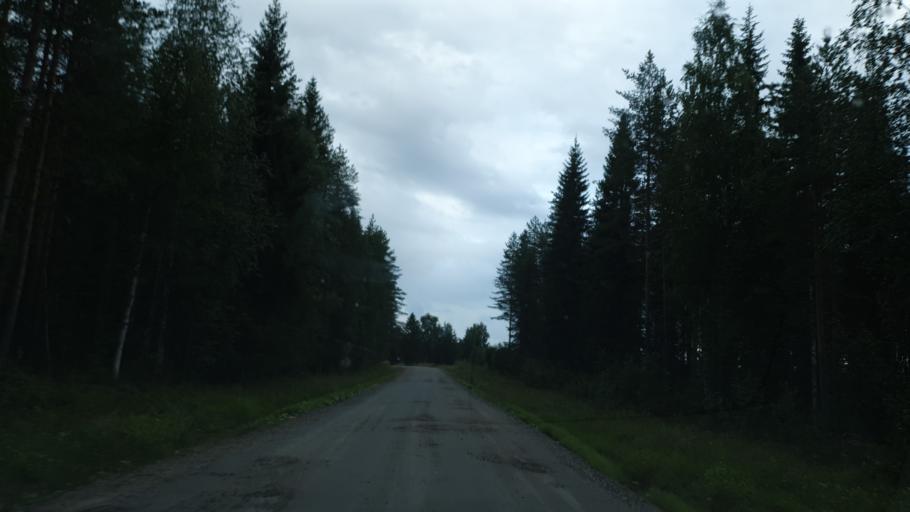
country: FI
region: Kainuu
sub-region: Kehys-Kainuu
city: Kuhmo
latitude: 64.2077
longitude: 29.3710
